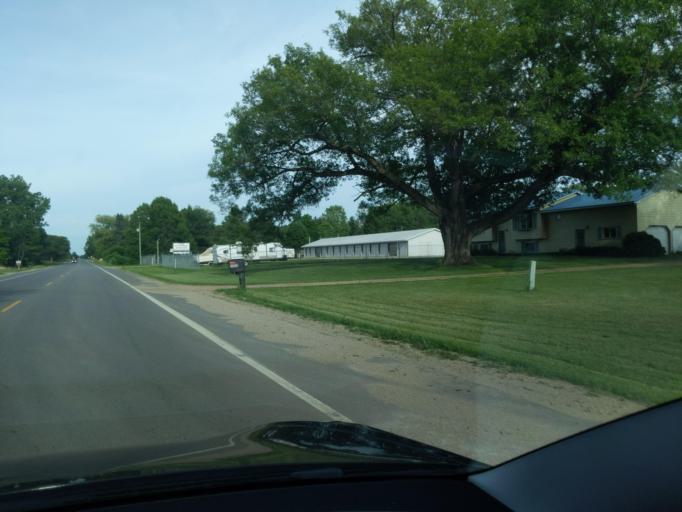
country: US
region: Michigan
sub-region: Montcalm County
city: Howard City
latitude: 43.3957
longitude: -85.4943
